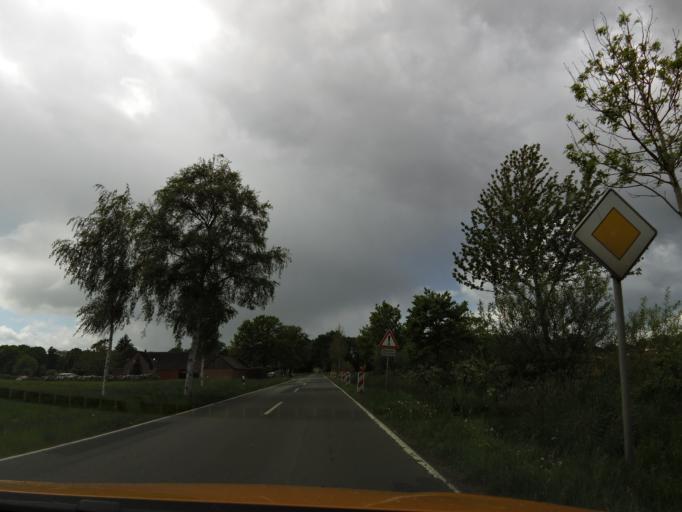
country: DE
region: Lower Saxony
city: Ganderkesee
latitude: 53.0153
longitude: 8.5851
